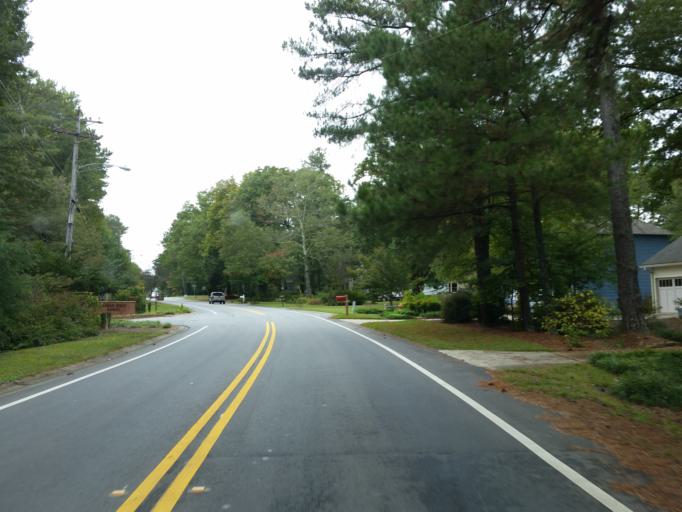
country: US
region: Georgia
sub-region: Fulton County
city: Roswell
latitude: 34.0047
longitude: -84.4505
